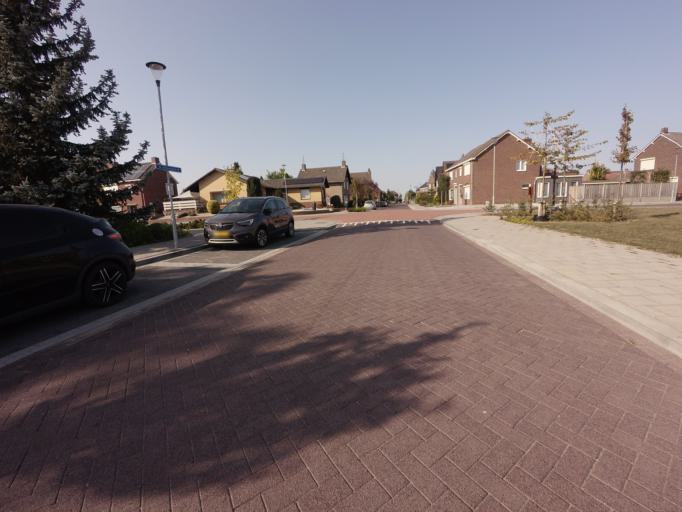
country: NL
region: Limburg
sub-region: Gemeente Maasgouw
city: Maasbracht
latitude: 51.1460
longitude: 5.8889
